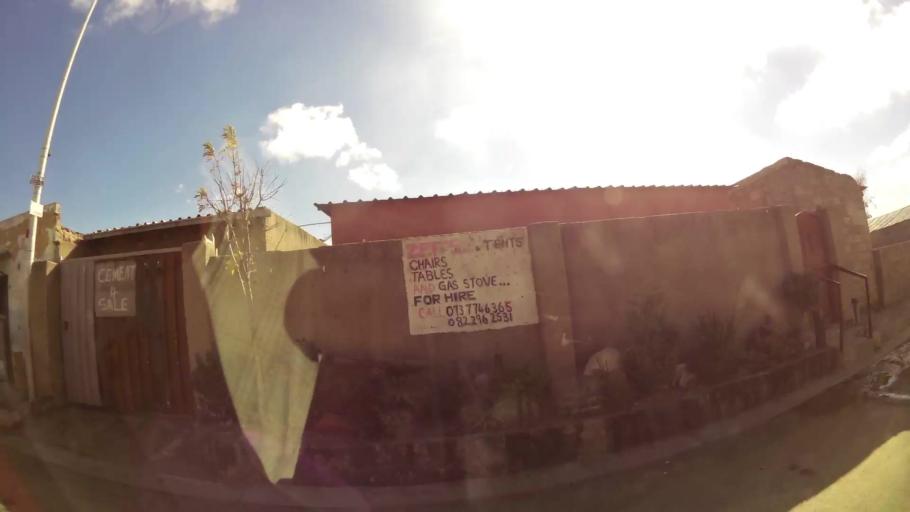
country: ZA
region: Gauteng
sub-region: City of Johannesburg Metropolitan Municipality
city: Modderfontein
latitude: -26.0420
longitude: 28.1791
